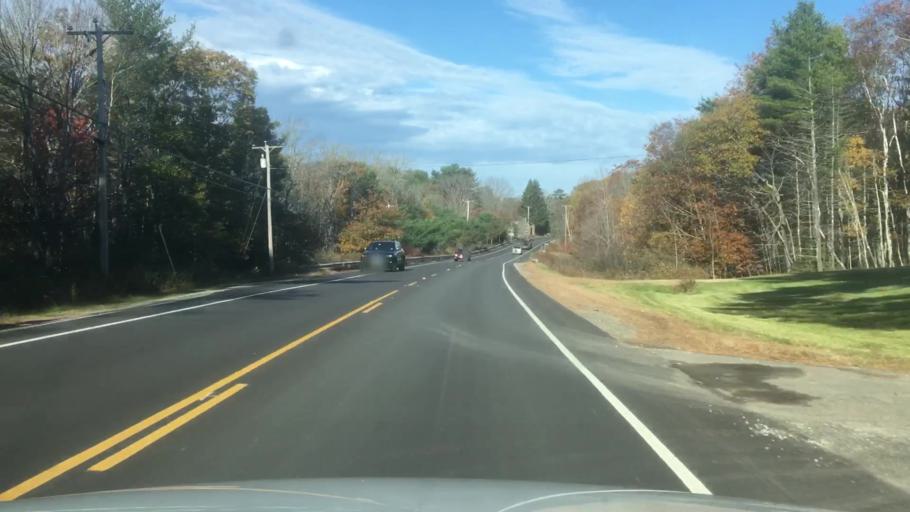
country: US
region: Maine
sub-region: Sagadahoc County
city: Woolwich
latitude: 43.8904
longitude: -69.7907
